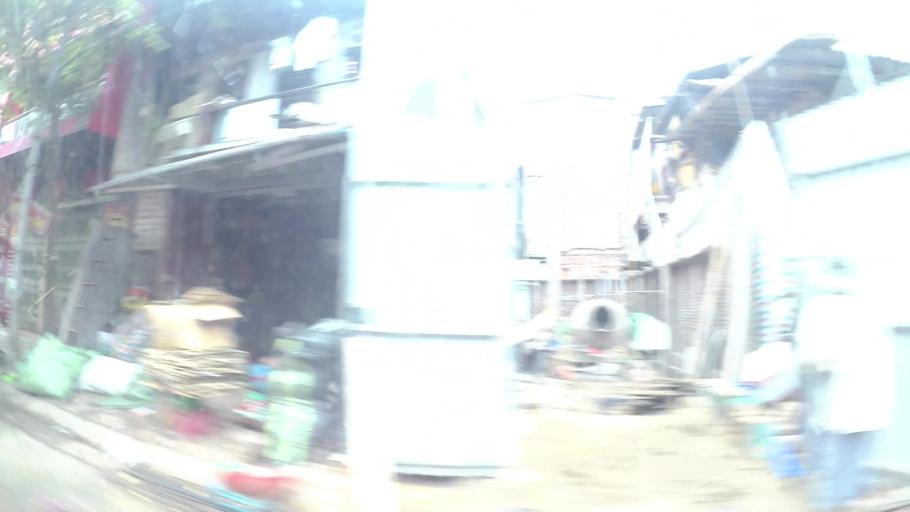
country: VN
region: Ha Noi
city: Dong Da
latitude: 21.0193
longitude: 105.8266
